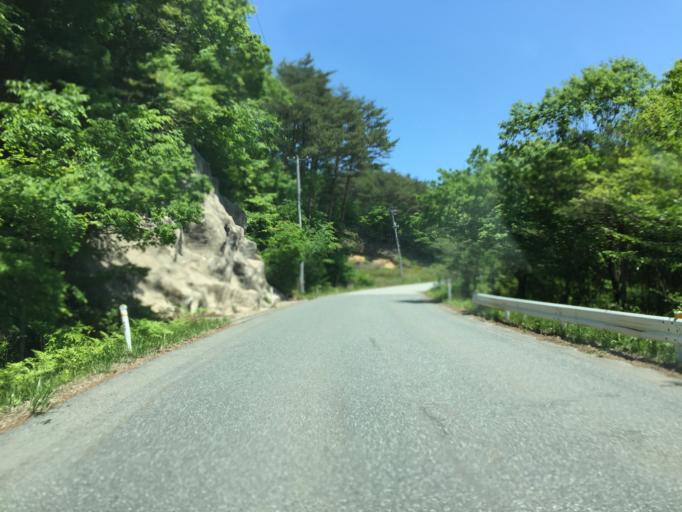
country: JP
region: Fukushima
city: Funehikimachi-funehiki
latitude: 37.5225
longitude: 140.7800
